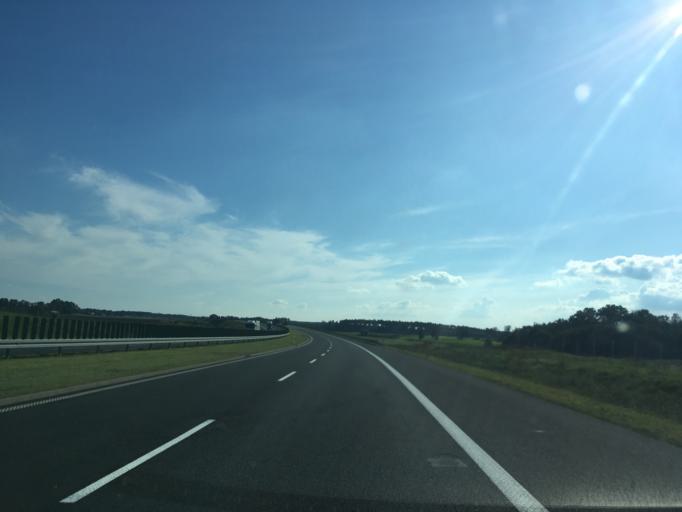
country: PL
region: Kujawsko-Pomorskie
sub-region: Powiat swiecki
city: Warlubie
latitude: 53.5771
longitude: 18.6055
